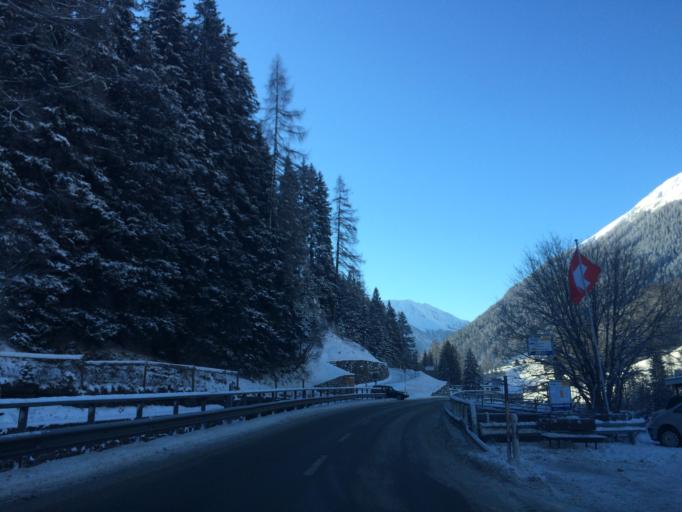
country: CH
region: Grisons
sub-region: Praettigau/Davos District
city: Davos
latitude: 46.7513
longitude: 9.7840
